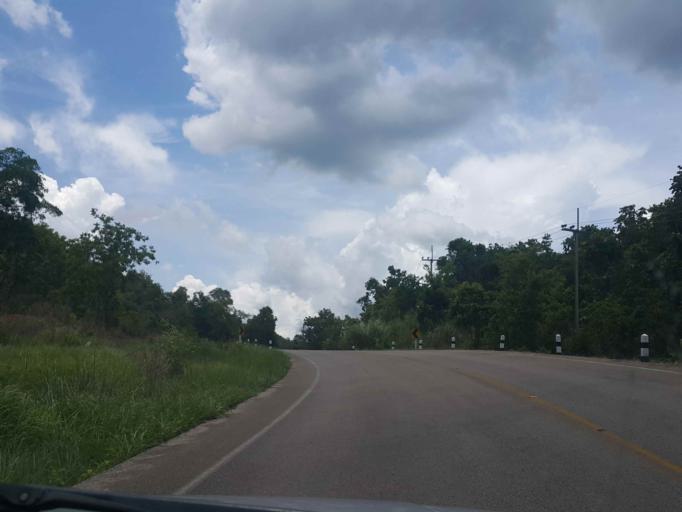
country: TH
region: Phayao
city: Chiang Muan
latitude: 18.9177
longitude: 100.1116
